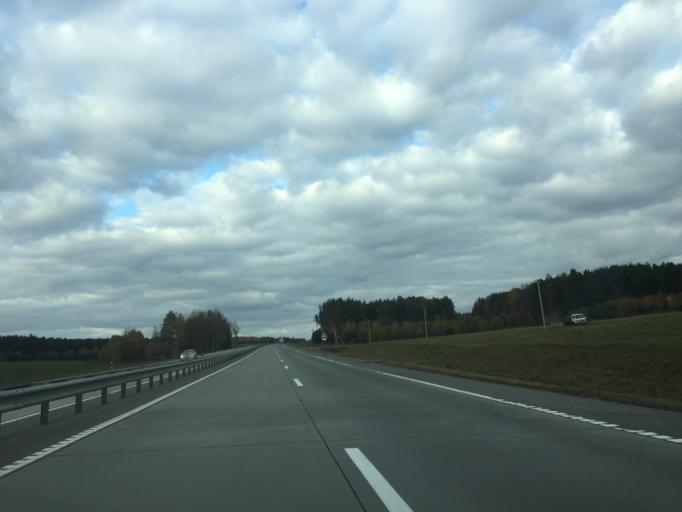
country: BY
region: Minsk
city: Rakaw
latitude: 53.9745
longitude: 27.0950
